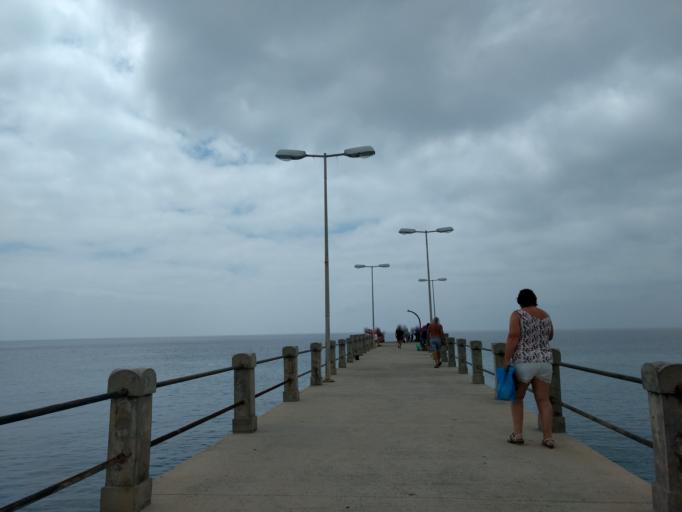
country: PT
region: Madeira
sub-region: Porto Santo
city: Vila de Porto Santo
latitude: 33.0569
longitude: -16.3342
